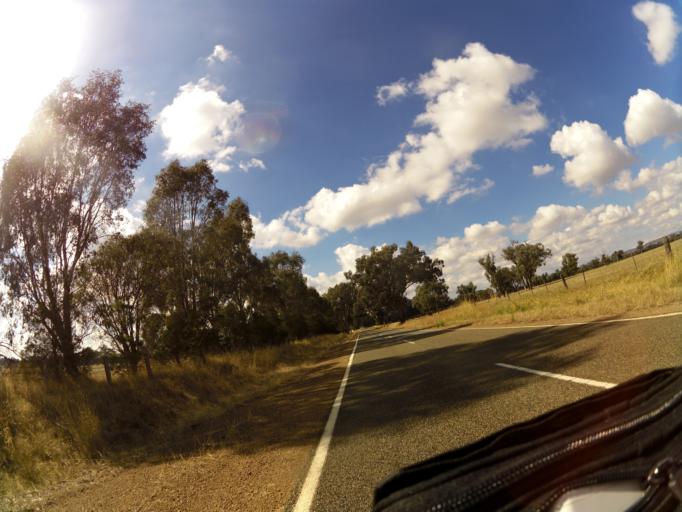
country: AU
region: Victoria
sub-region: Benalla
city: Benalla
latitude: -36.6109
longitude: 146.0206
